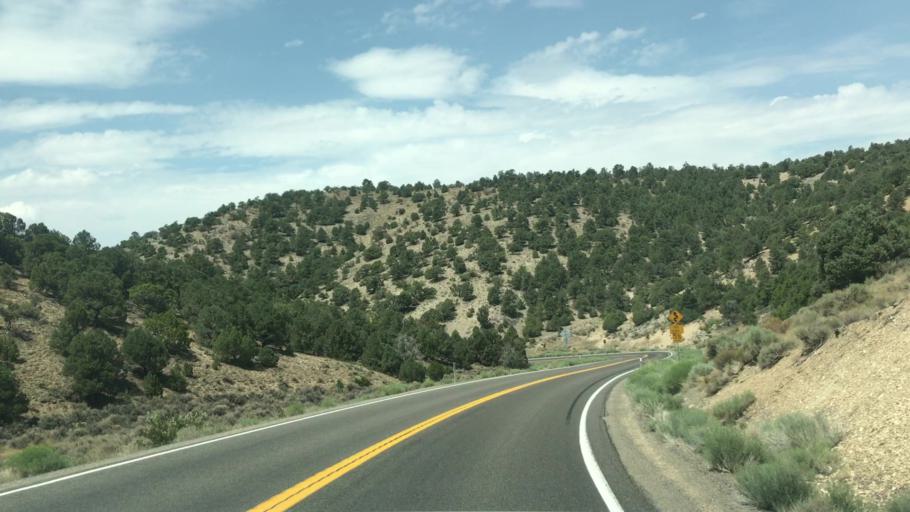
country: US
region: Nevada
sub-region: Eureka County
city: Eureka
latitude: 39.3945
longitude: -115.4848
